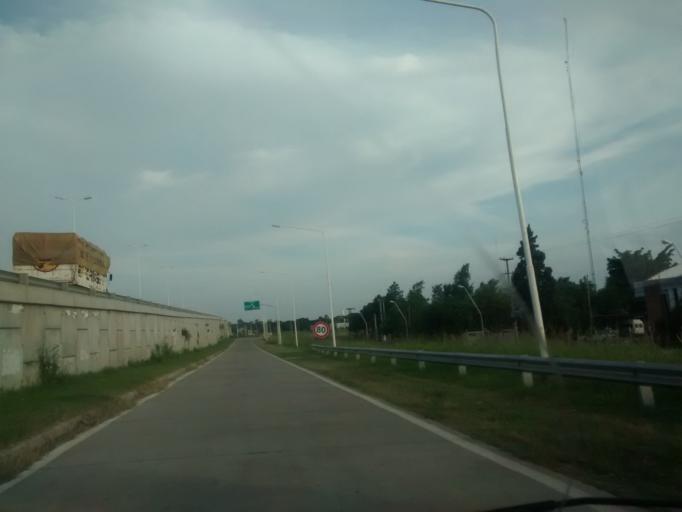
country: AR
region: Chaco
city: Resistencia
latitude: -27.4197
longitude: -58.9598
